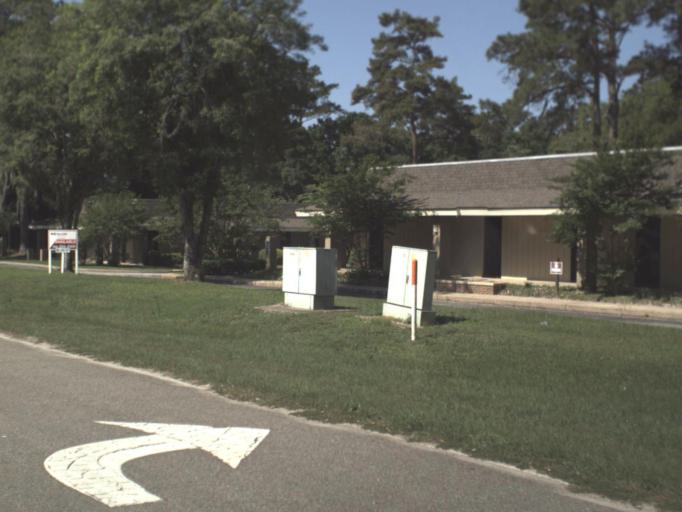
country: US
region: Florida
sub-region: Leon County
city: Tallahassee
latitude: 30.4515
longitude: -84.3458
